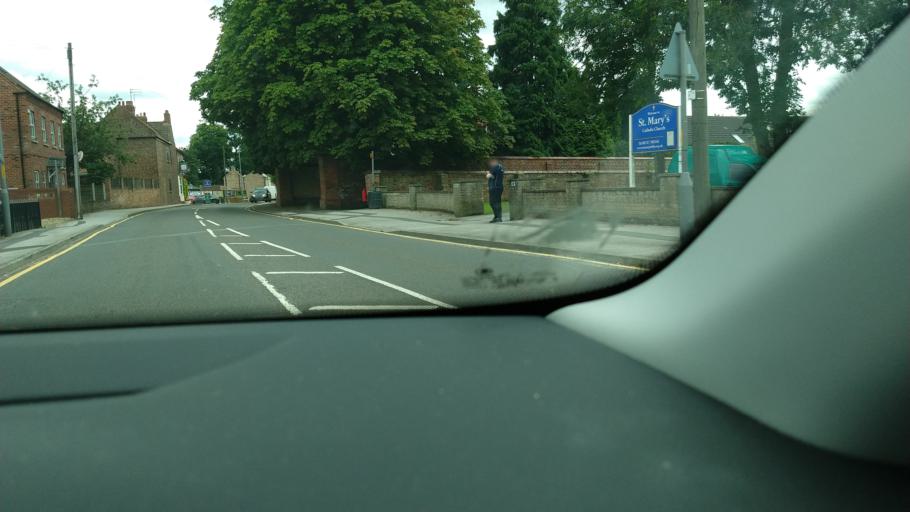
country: GB
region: England
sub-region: North Yorkshire
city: Camblesforth
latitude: 53.7112
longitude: -1.0198
